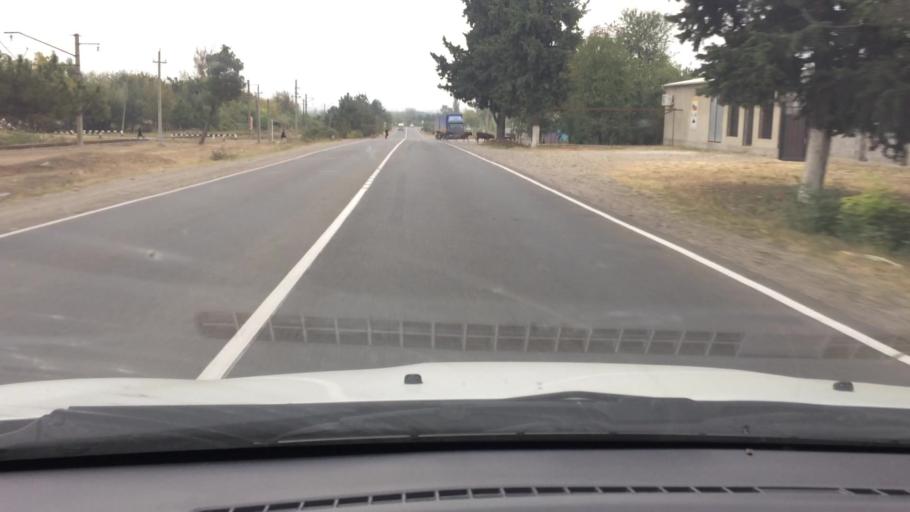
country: GE
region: Kvemo Kartli
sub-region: Marneuli
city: Marneuli
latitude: 41.4133
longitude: 44.8287
